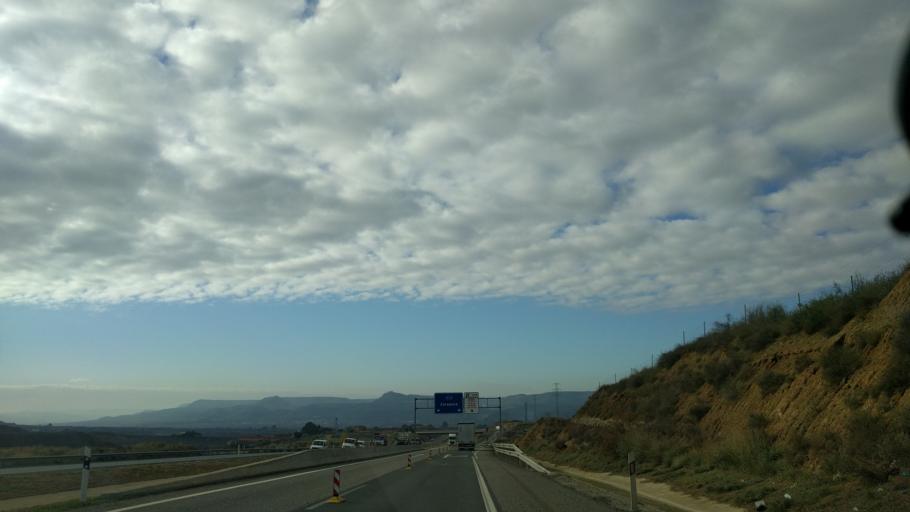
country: ES
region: Aragon
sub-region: Provincia de Huesca
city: Fraga
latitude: 41.5178
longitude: 0.3737
